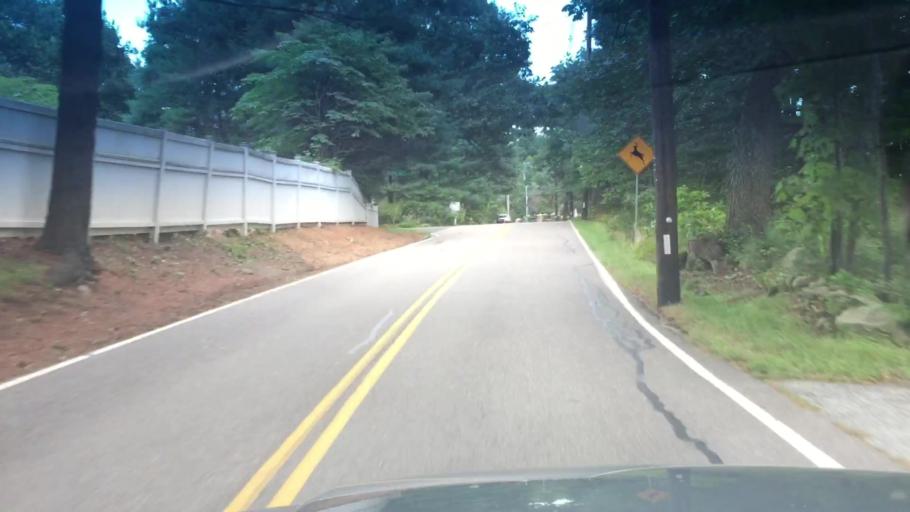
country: US
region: Massachusetts
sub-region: Norfolk County
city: Westwood
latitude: 42.2090
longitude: -71.2221
